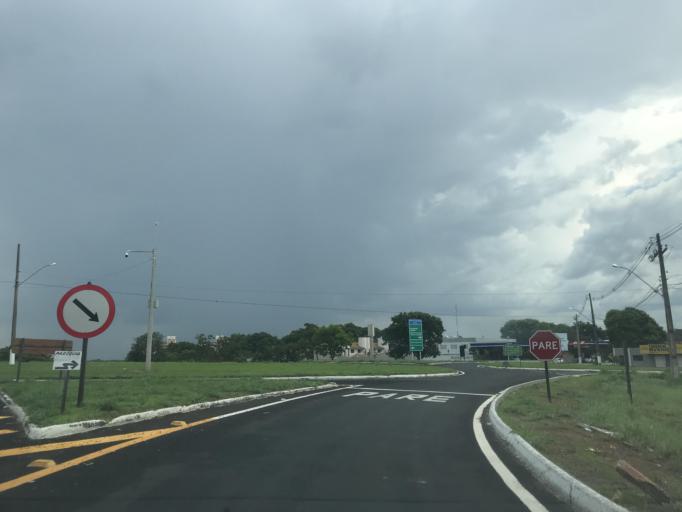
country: BR
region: Goias
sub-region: Caldas Novas
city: Caldas Novas
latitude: -17.7659
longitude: -48.7561
